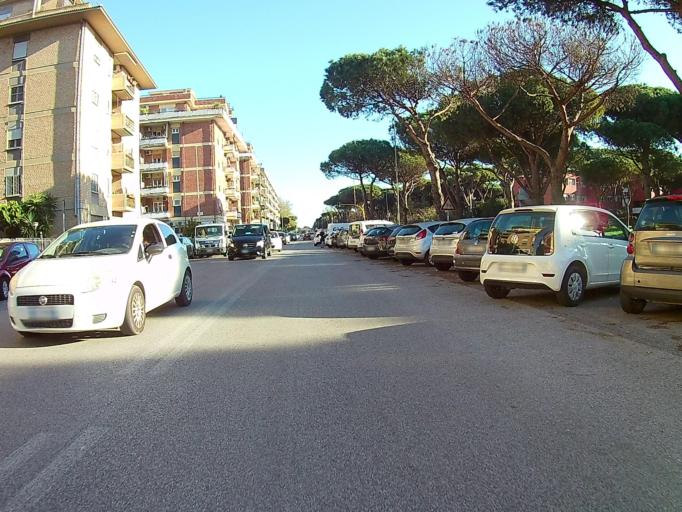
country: IT
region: Latium
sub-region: Citta metropolitana di Roma Capitale
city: Lido di Ostia
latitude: 41.7351
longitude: 12.2948
